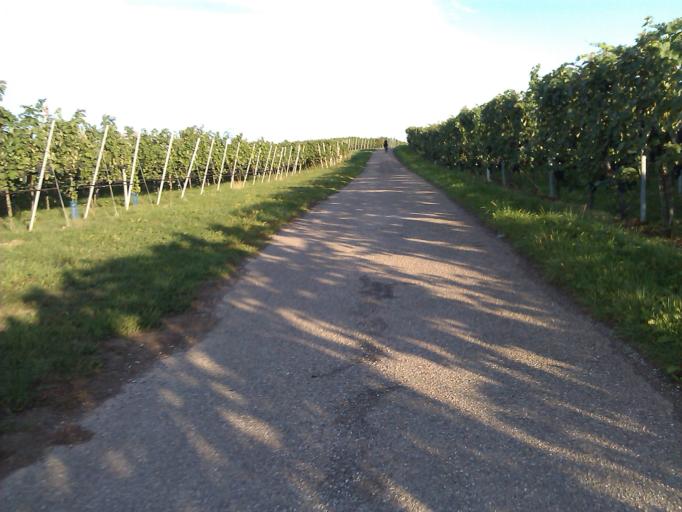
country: DE
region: Baden-Wuerttemberg
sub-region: Regierungsbezirk Stuttgart
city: Lauffen am Neckar
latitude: 49.0972
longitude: 9.1604
